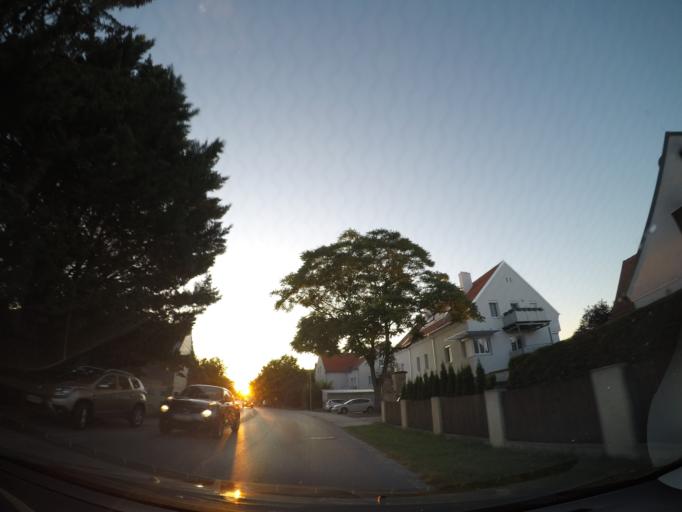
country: AT
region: Lower Austria
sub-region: Politischer Bezirk Baden
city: Seibersdorf
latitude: 47.9586
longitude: 16.5225
